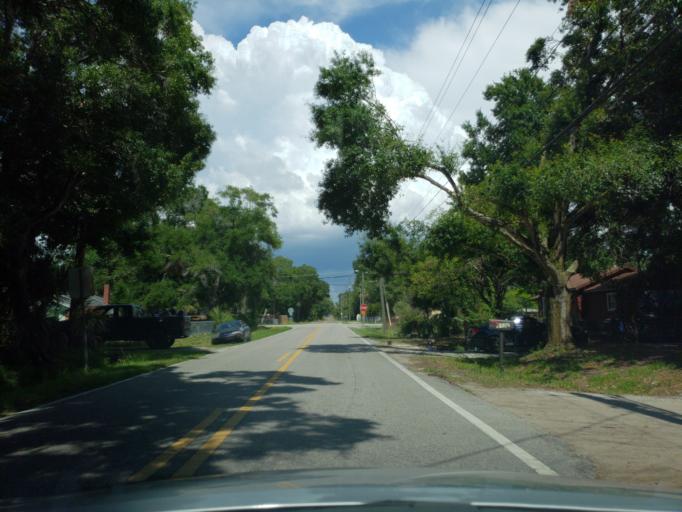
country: US
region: Florida
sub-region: Hillsborough County
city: Palm River-Clair Mel
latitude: 27.9335
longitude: -82.3858
